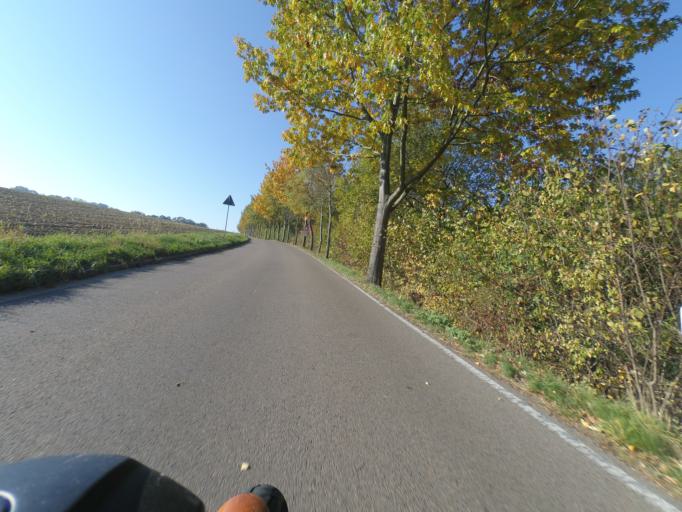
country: DE
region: Saxony
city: Rabenau
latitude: 50.9618
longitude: 13.6310
